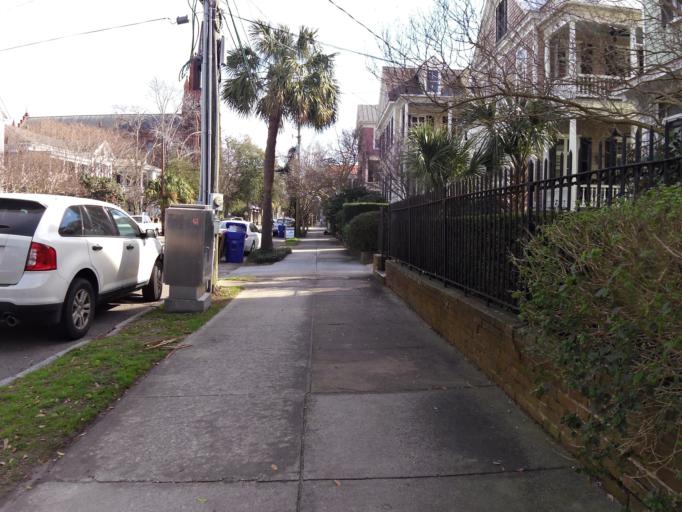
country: US
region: South Carolina
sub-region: Charleston County
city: Charleston
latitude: 32.7759
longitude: -79.9356
